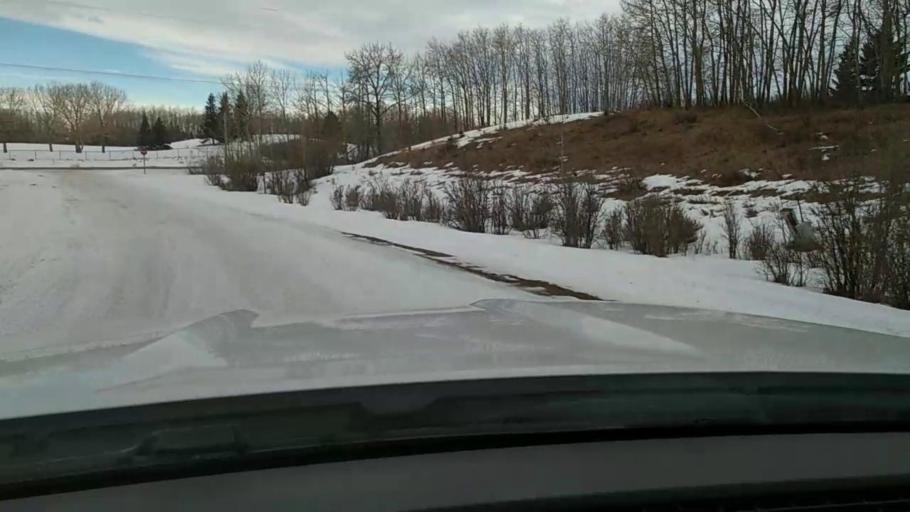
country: CA
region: Alberta
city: Calgary
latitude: 51.1591
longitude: -114.2559
